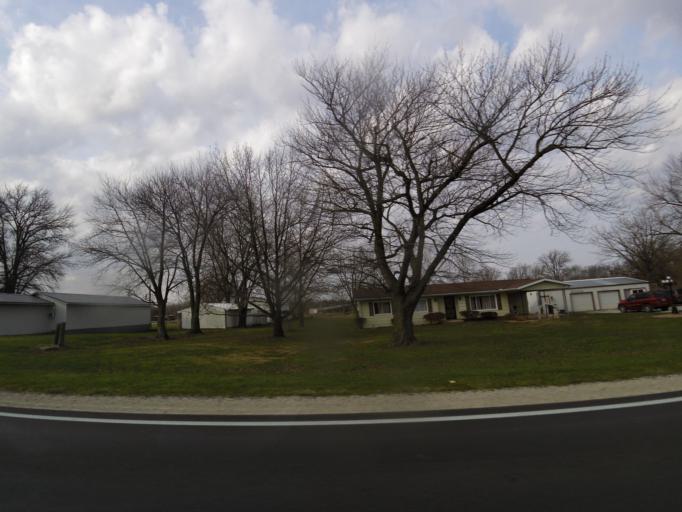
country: US
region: Illinois
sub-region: Christian County
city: Pana
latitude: 39.3746
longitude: -89.0817
